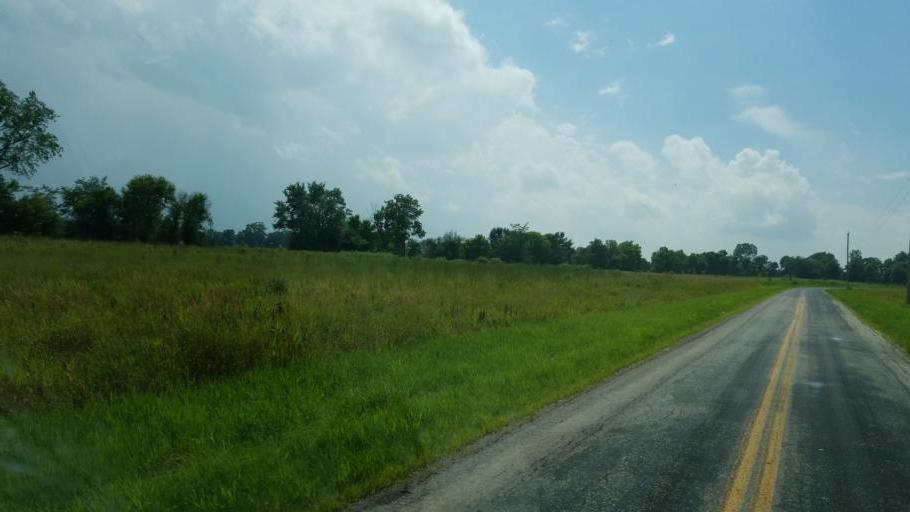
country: US
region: Ohio
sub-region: Union County
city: Richwood
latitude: 40.5591
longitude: -83.3369
